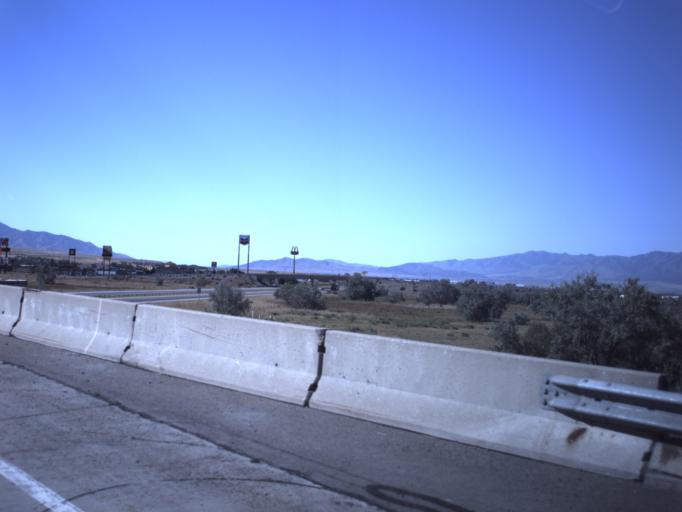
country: US
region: Utah
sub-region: Tooele County
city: Stansbury park
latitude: 40.6943
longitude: -112.2641
